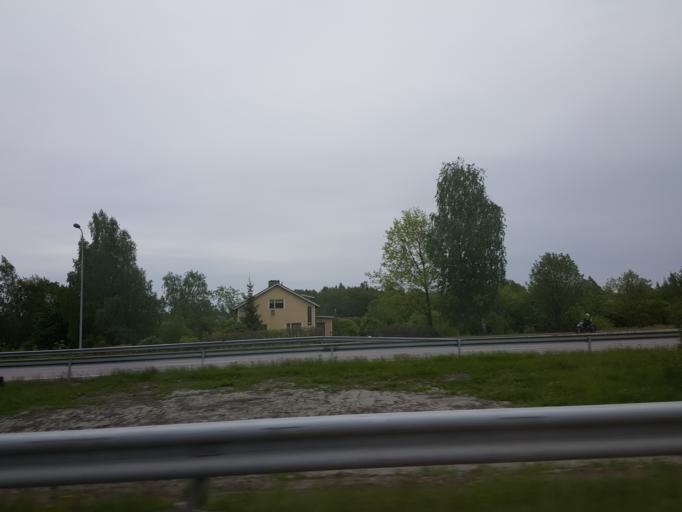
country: FI
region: Uusimaa
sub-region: Helsinki
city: Vantaa
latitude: 60.2739
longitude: 24.9755
